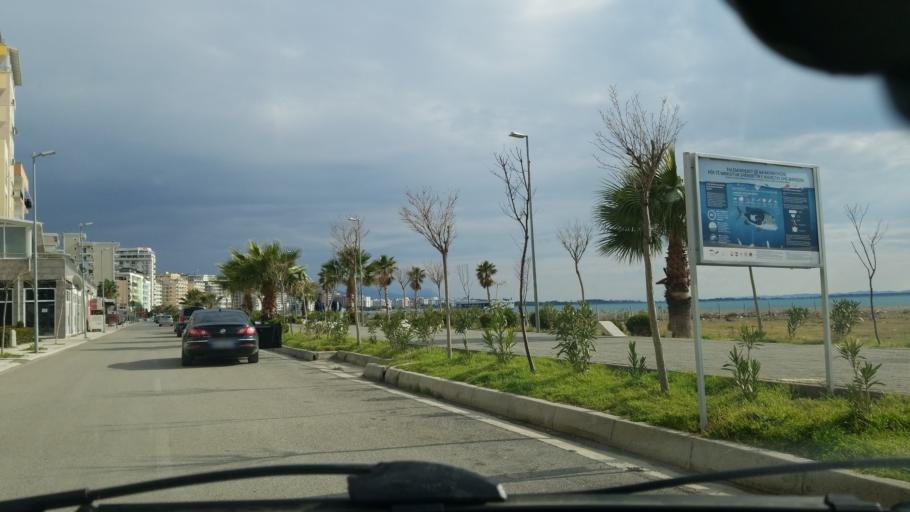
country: AL
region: Lezhe
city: Shengjin
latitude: 41.8131
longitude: 19.5918
